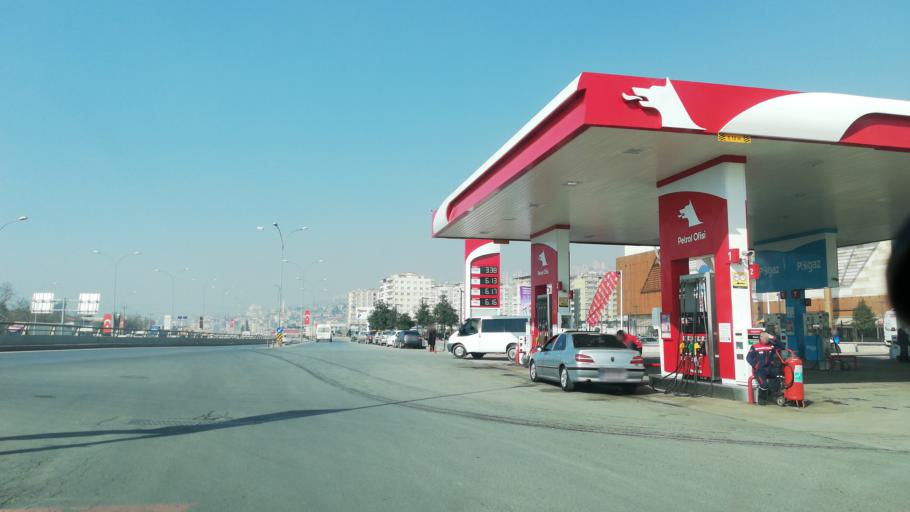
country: TR
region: Kahramanmaras
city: Kahramanmaras
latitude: 37.5691
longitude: 36.9232
